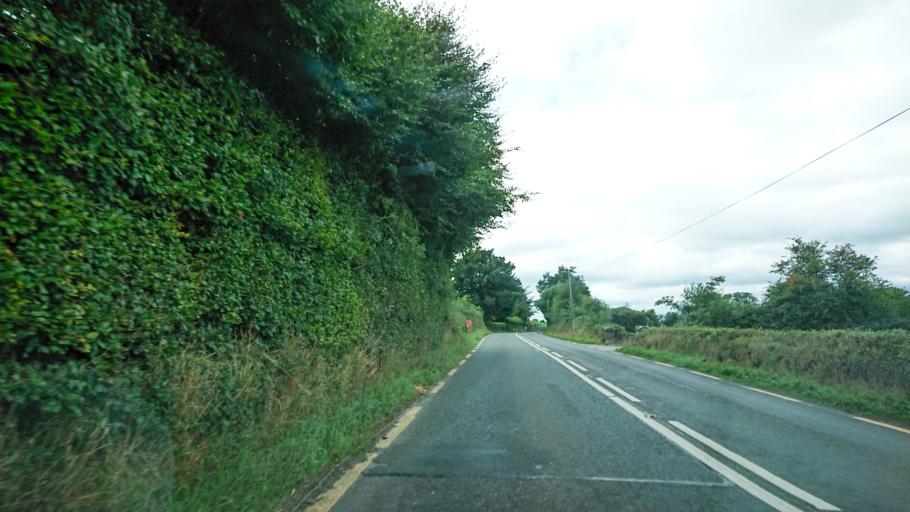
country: IE
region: Munster
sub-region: Waterford
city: Dungarvan
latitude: 52.1117
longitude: -7.6978
